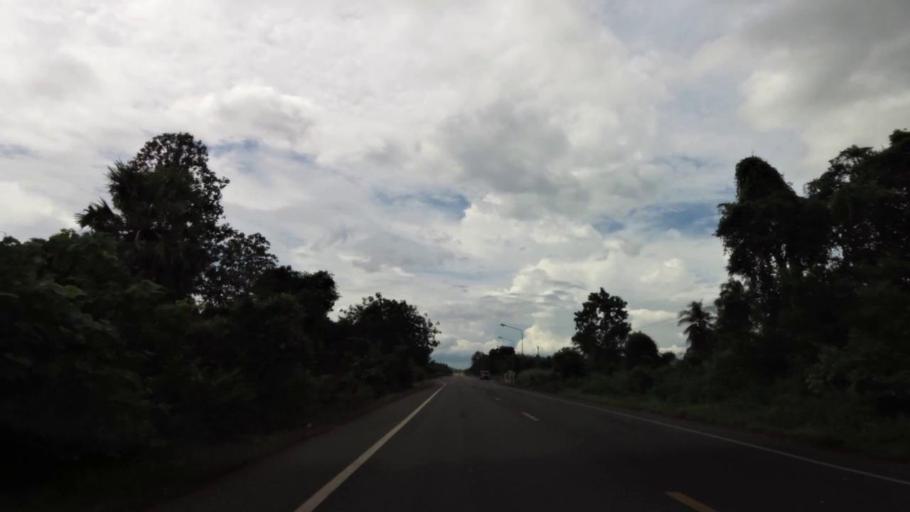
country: TH
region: Nakhon Sawan
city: Phai Sali
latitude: 15.5993
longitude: 100.6711
